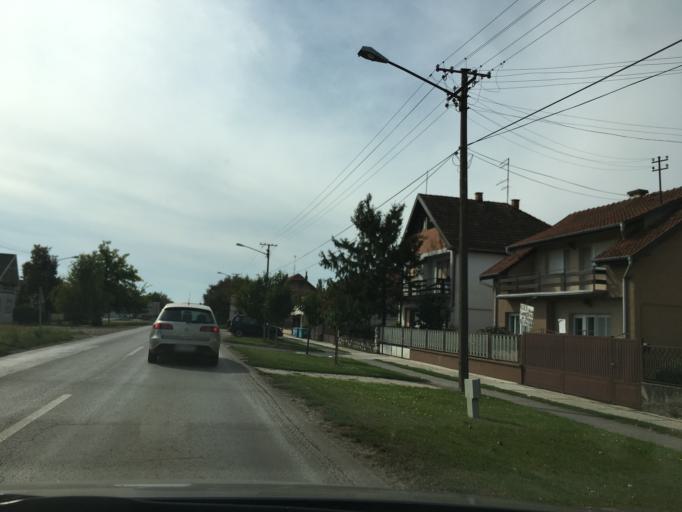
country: RS
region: Autonomna Pokrajina Vojvodina
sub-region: Juznobacki Okrug
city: Temerin
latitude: 45.4323
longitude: 19.8977
